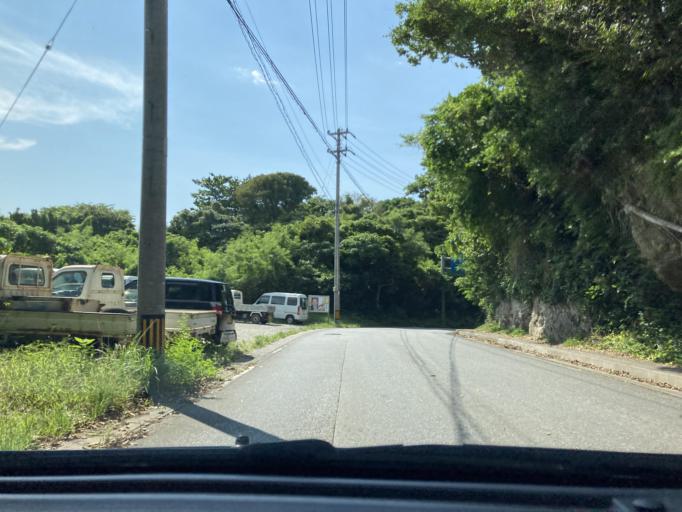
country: JP
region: Okinawa
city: Tomigusuku
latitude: 26.1421
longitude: 127.7681
